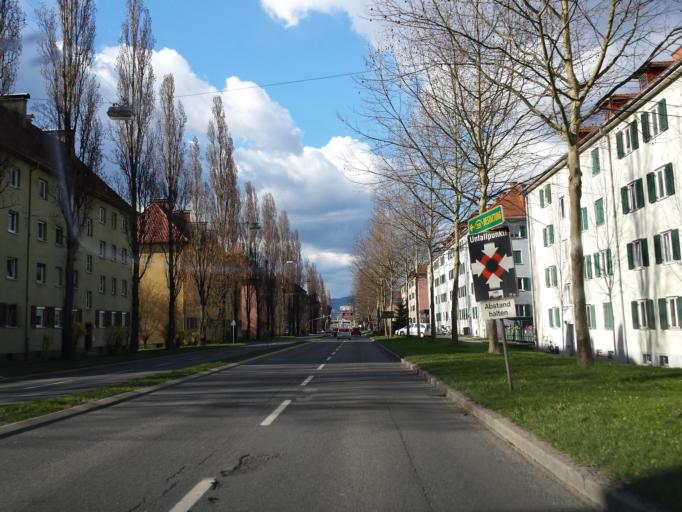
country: AT
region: Styria
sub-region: Graz Stadt
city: Graz
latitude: 47.0501
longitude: 15.4289
